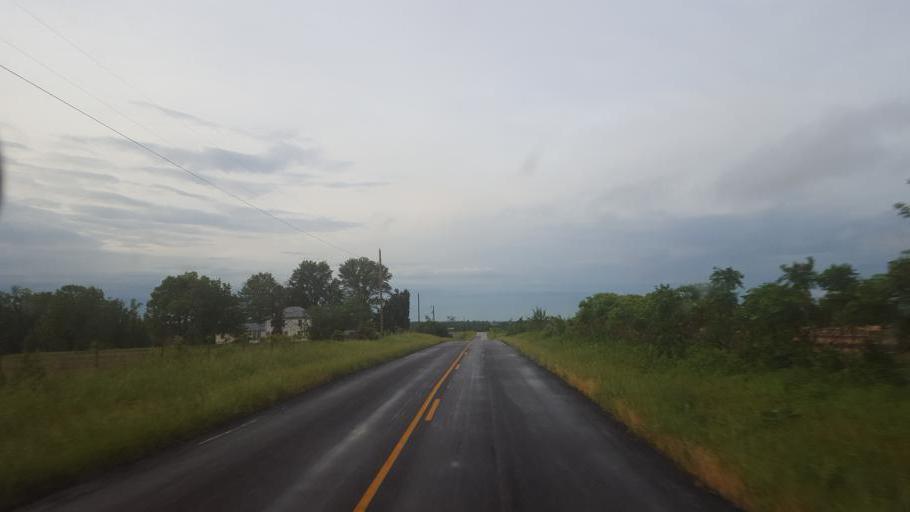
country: US
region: Missouri
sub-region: Moniteau County
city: California
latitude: 38.6774
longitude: -92.5864
